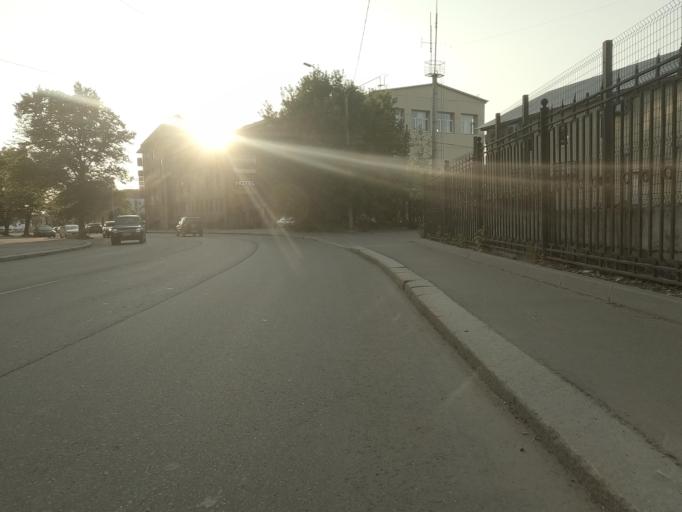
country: RU
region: Leningrad
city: Vyborg
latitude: 60.7146
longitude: 28.7551
